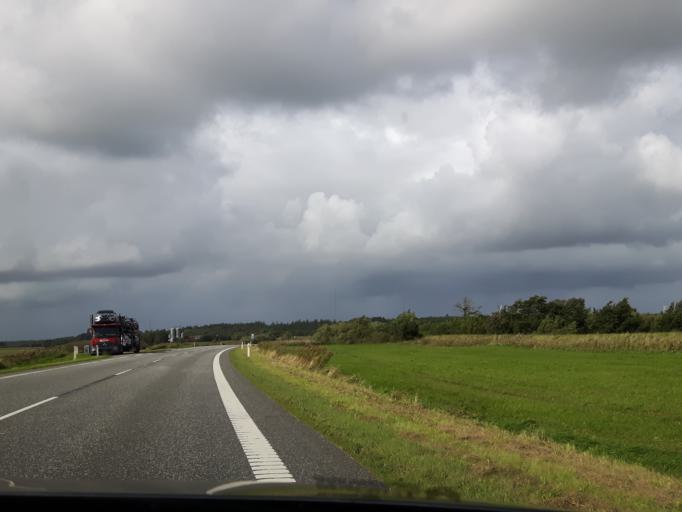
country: DK
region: North Denmark
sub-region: Morso Kommune
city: Nykobing Mors
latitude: 57.0348
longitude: 8.9393
